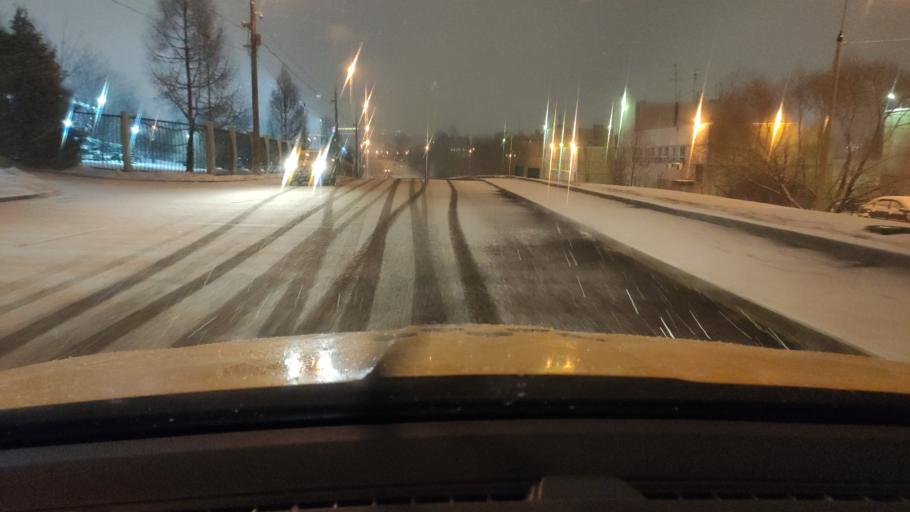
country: RU
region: Moskovskaya
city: Kastanayevo
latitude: 55.7271
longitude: 37.5057
